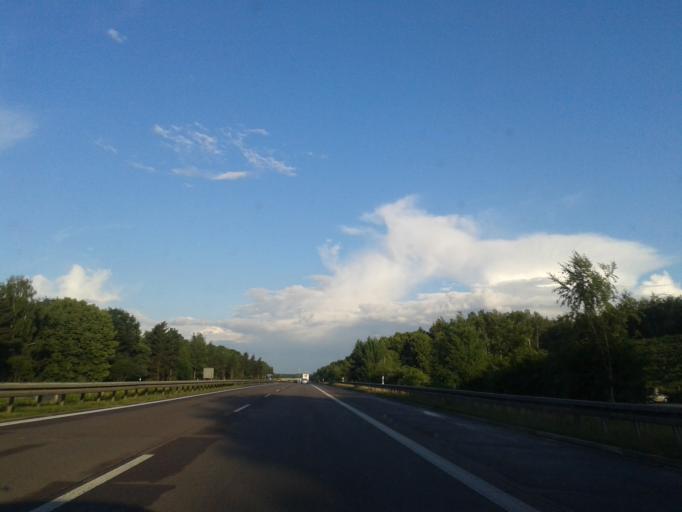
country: DE
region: Saxony
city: Naunhof
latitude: 51.2988
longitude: 12.6140
